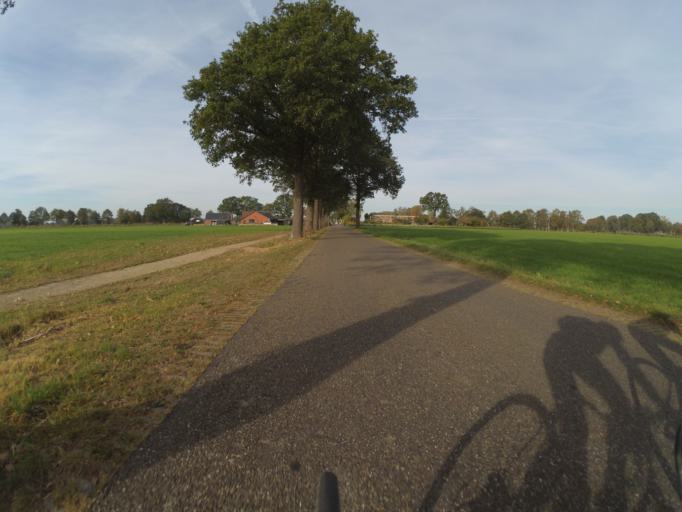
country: NL
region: Overijssel
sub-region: Gemeente Raalte
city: Raalte
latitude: 52.3272
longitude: 6.2672
